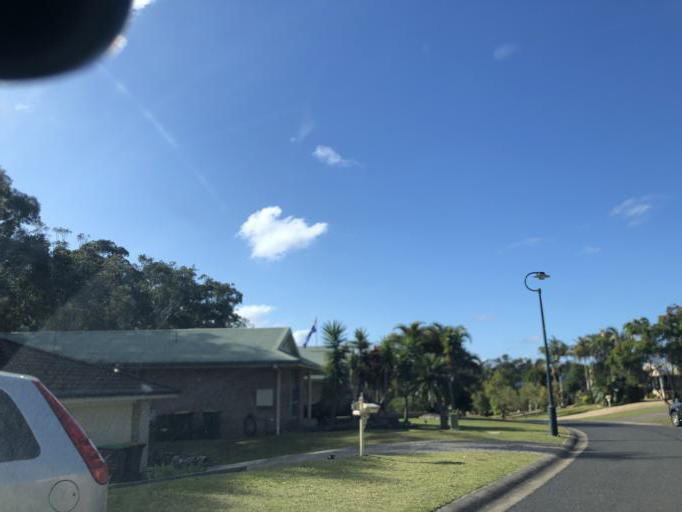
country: AU
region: New South Wales
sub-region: Coffs Harbour
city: Woolgoolga
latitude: -30.0953
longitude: 153.1960
